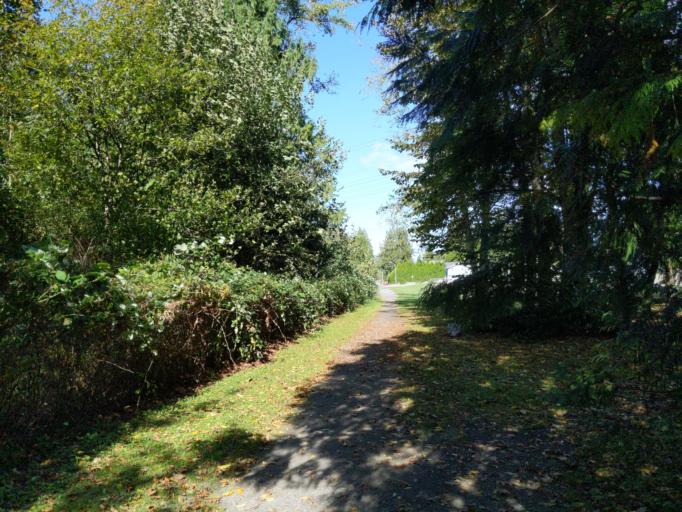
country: CA
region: British Columbia
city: Langley
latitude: 49.0882
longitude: -122.6796
